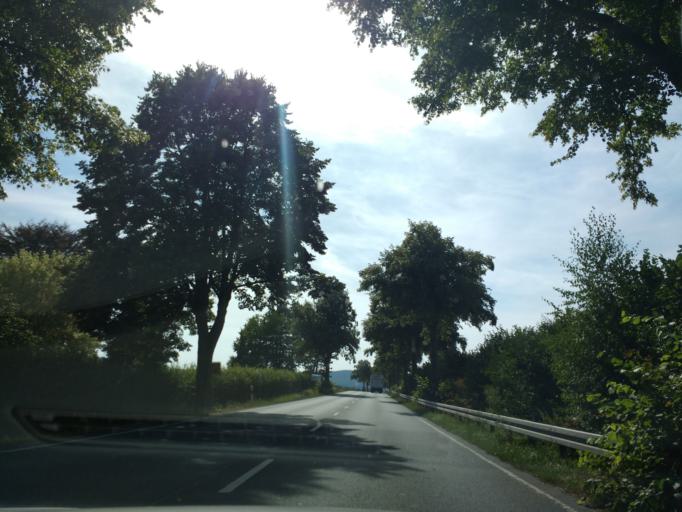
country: DE
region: Lower Saxony
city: Heinsen
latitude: 52.0884
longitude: 9.6305
